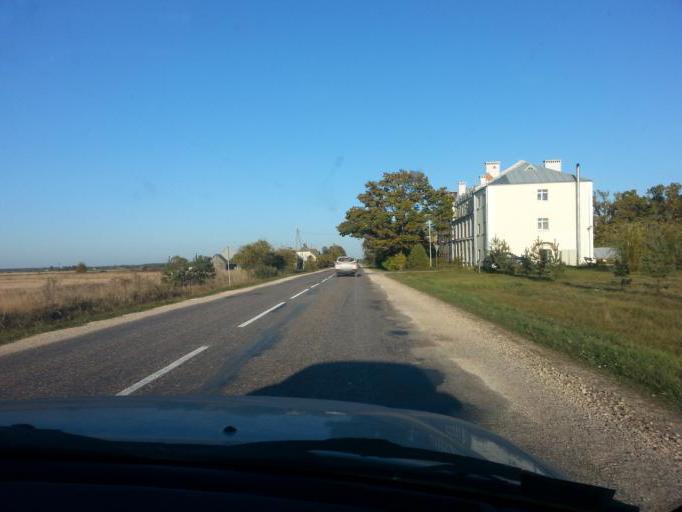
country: LV
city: Tervete
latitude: 56.6000
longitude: 23.4923
